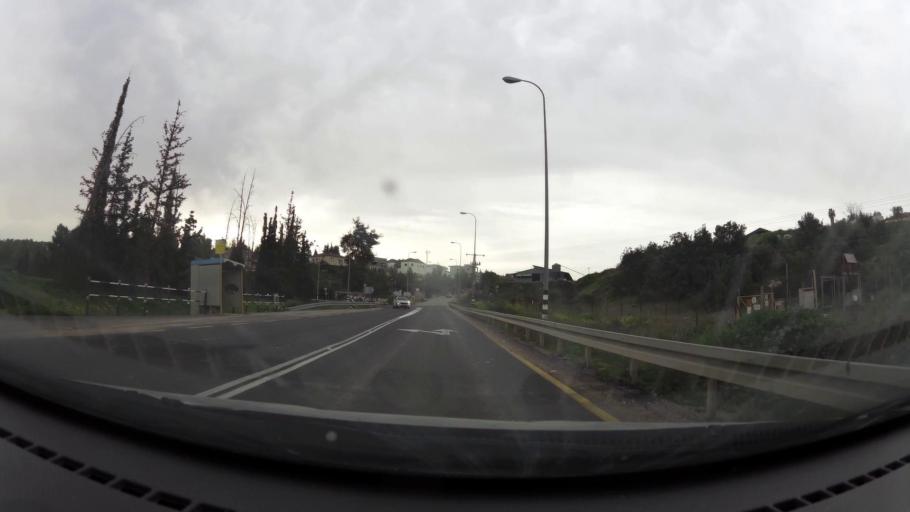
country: PS
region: West Bank
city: Surif
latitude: 31.6748
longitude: 35.0110
